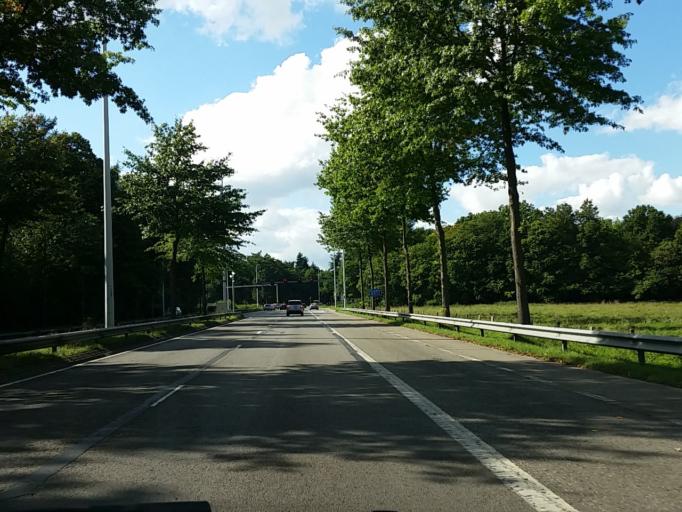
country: BE
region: Flanders
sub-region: Provincie Antwerpen
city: Wijnegem
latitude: 51.2340
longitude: 4.5374
